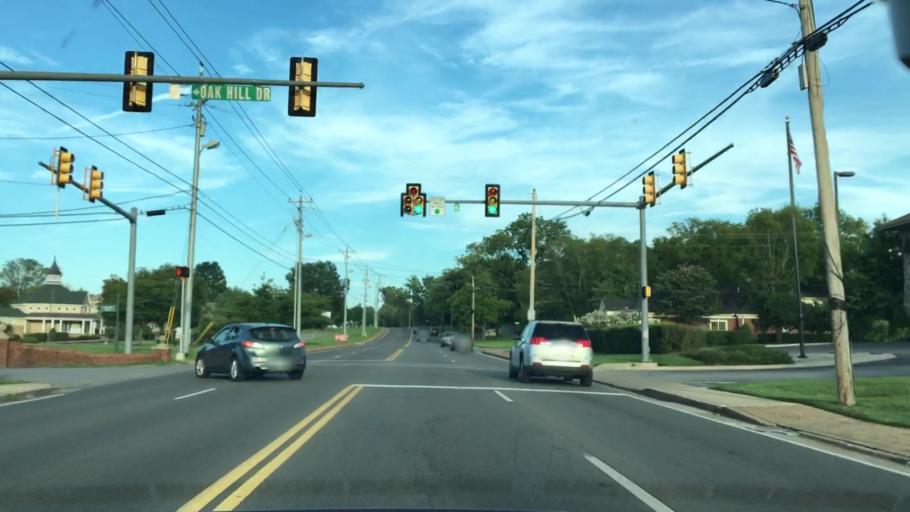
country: US
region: Tennessee
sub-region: Wilson County
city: Lebanon
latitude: 36.2106
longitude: -86.3119
